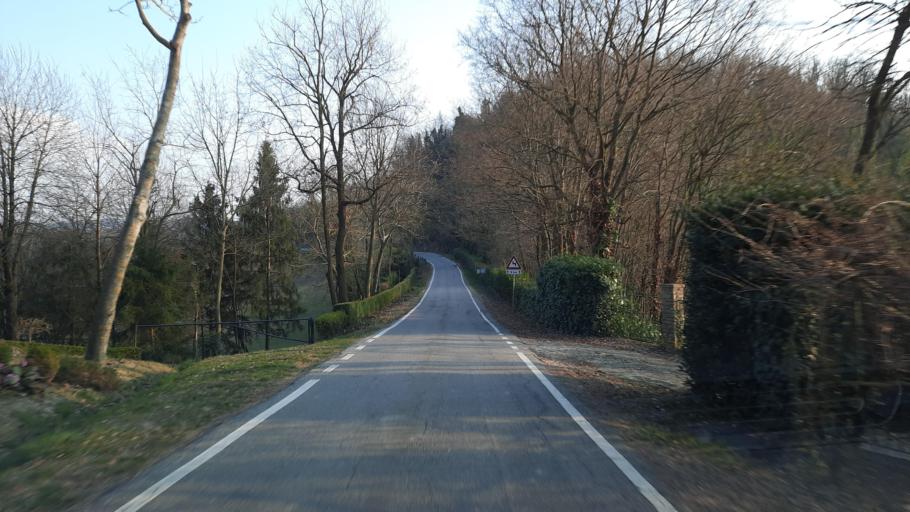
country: IT
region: Piedmont
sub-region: Provincia di Alessandria
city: Odalengo Grande
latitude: 45.1065
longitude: 8.1704
